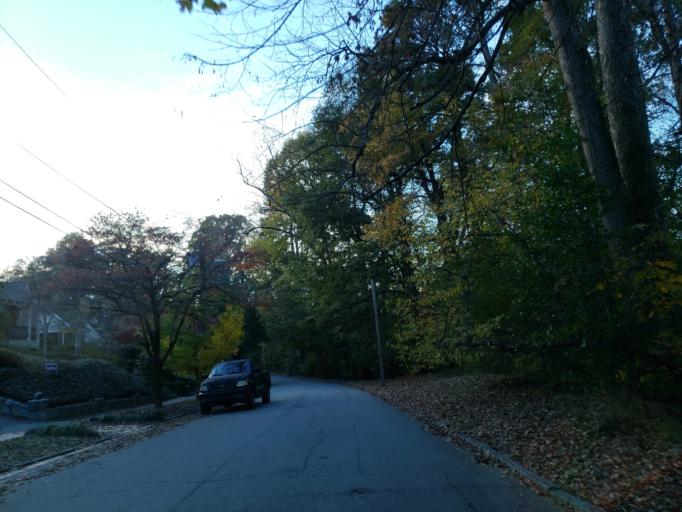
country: US
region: Georgia
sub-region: DeKalb County
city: Druid Hills
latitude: 33.7850
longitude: -84.3606
